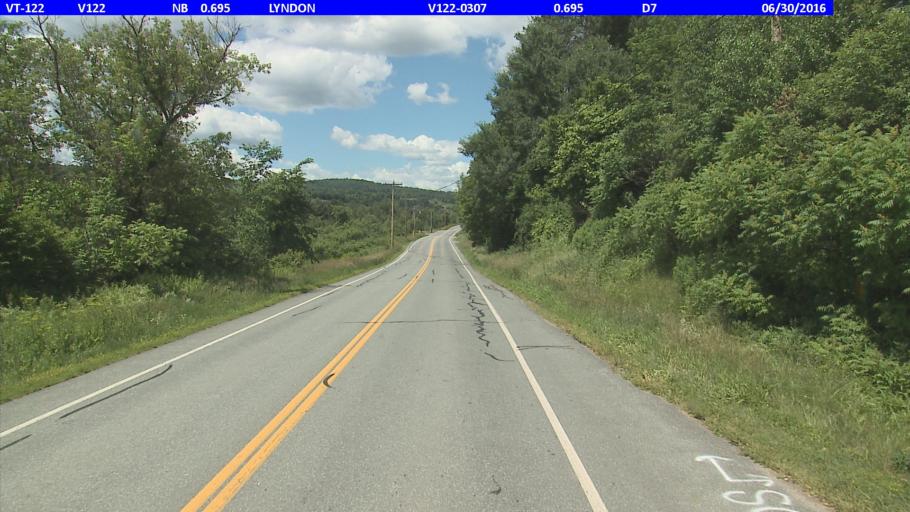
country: US
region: Vermont
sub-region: Caledonia County
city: Lyndonville
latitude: 44.5439
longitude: -72.0125
